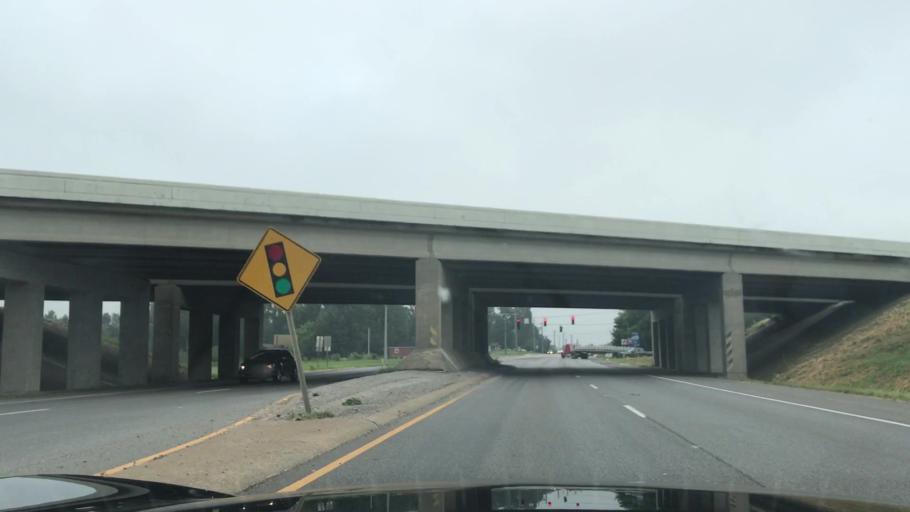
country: US
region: Kentucky
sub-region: Graves County
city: Mayfield
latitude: 36.7676
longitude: -88.6432
